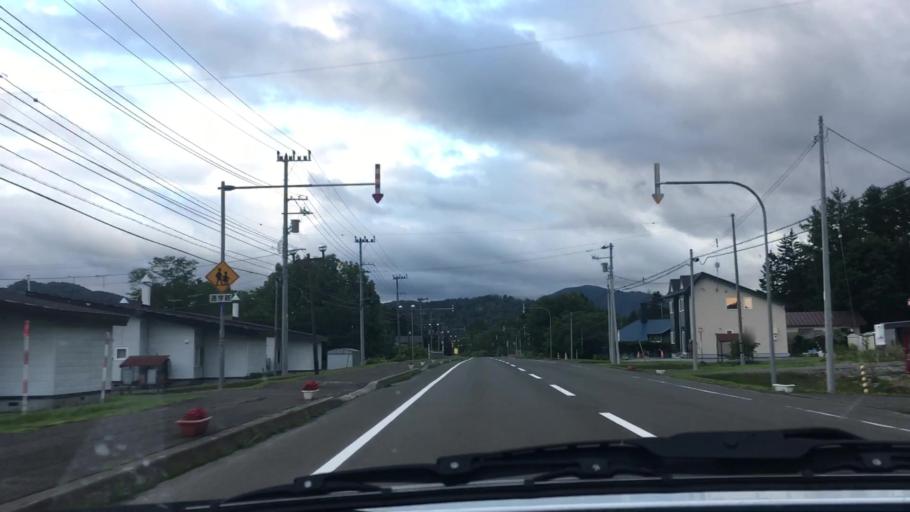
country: JP
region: Hokkaido
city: Shimo-furano
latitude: 42.9910
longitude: 142.4003
